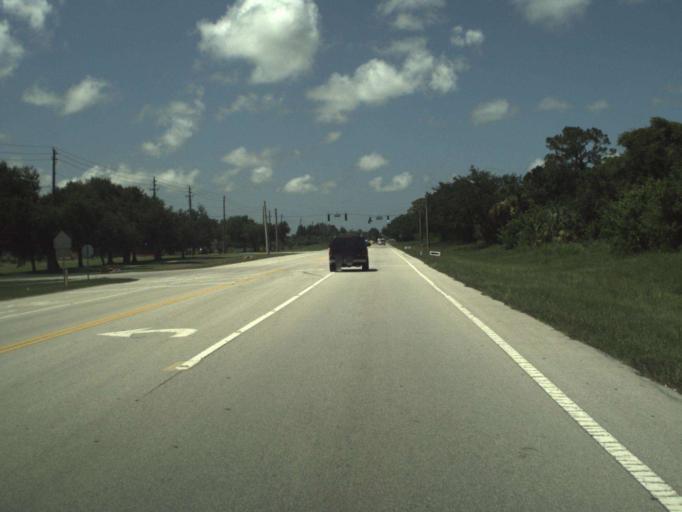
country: US
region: Florida
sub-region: Indian River County
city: Sebastian
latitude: 27.7570
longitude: -80.5112
